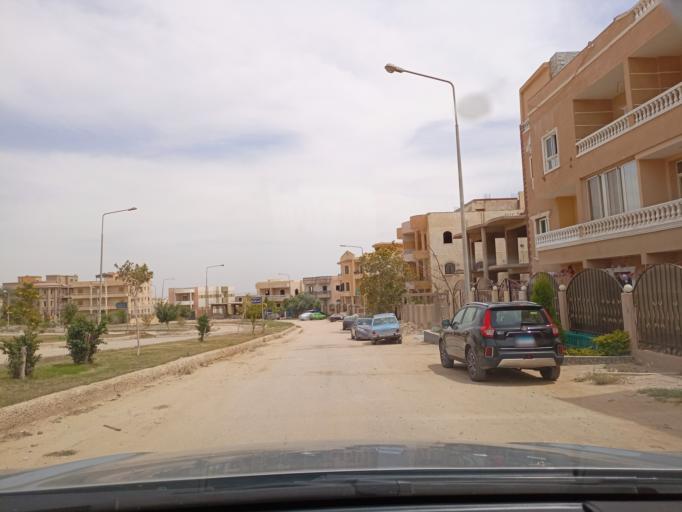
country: EG
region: Muhafazat al Qalyubiyah
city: Al Khankah
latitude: 30.2385
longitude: 31.4886
